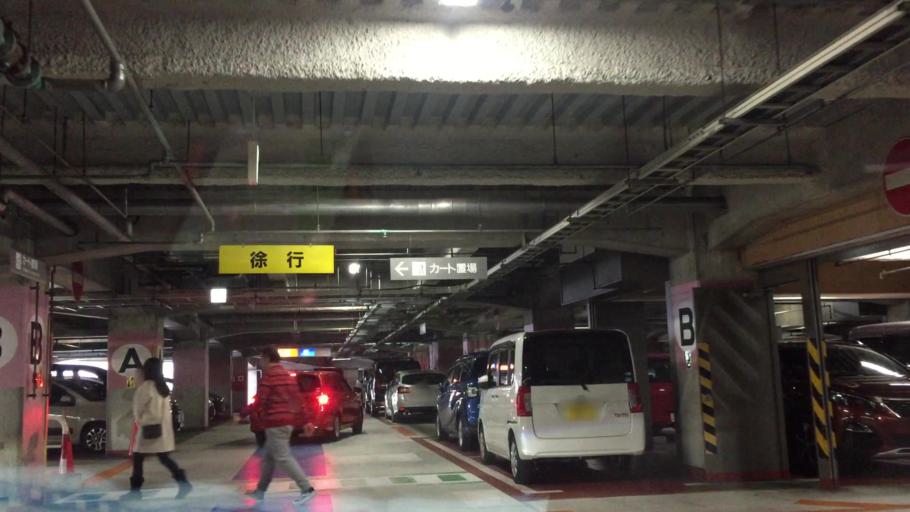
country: JP
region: Kanagawa
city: Zushi
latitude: 35.3351
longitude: 139.6241
